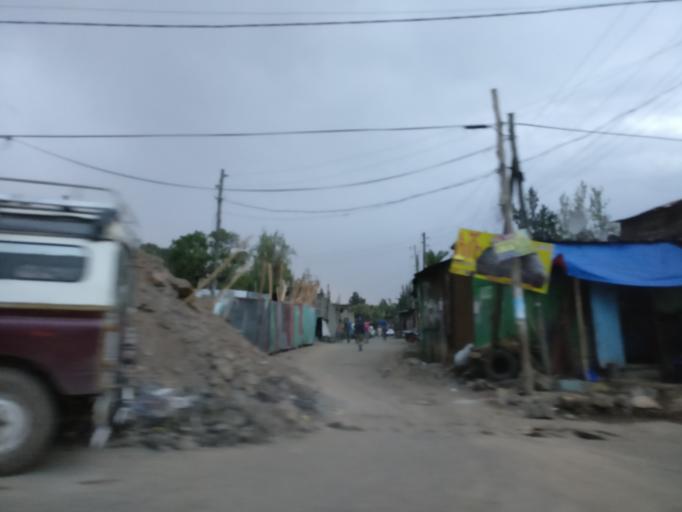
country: ET
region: Adis Abeba
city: Addis Ababa
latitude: 9.0165
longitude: 38.7387
